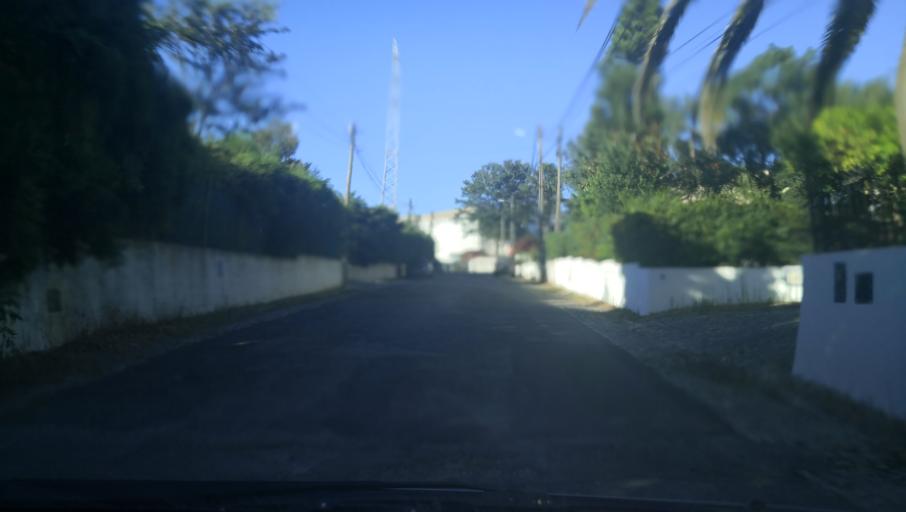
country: PT
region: Setubal
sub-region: Palmela
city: Palmela
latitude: 38.5523
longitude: -8.8872
